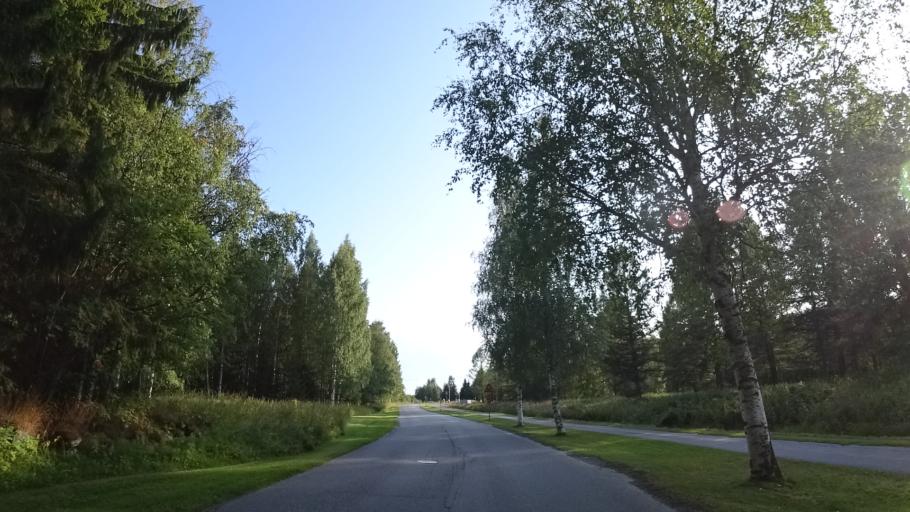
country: FI
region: North Karelia
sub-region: Pielisen Karjala
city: Lieksa
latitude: 63.3122
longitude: 30.0264
